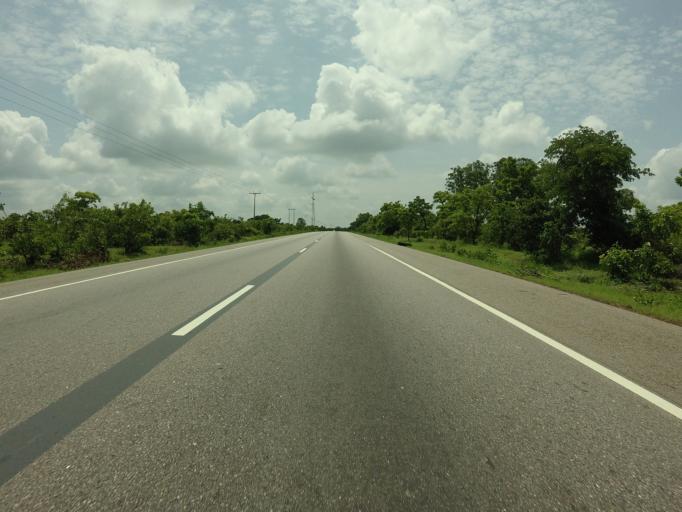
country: GH
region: Northern
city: Tamale
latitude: 9.1282
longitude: -1.2509
